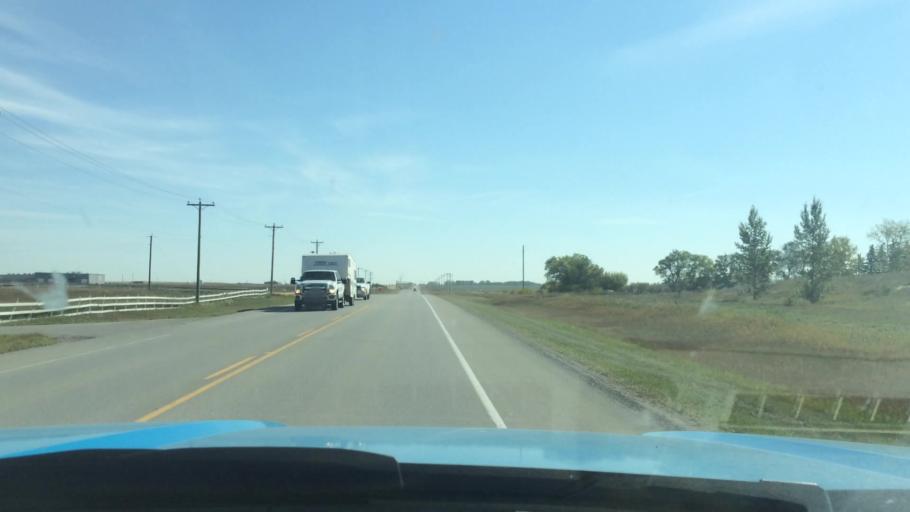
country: CA
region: Alberta
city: Airdrie
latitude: 51.2126
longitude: -113.9486
